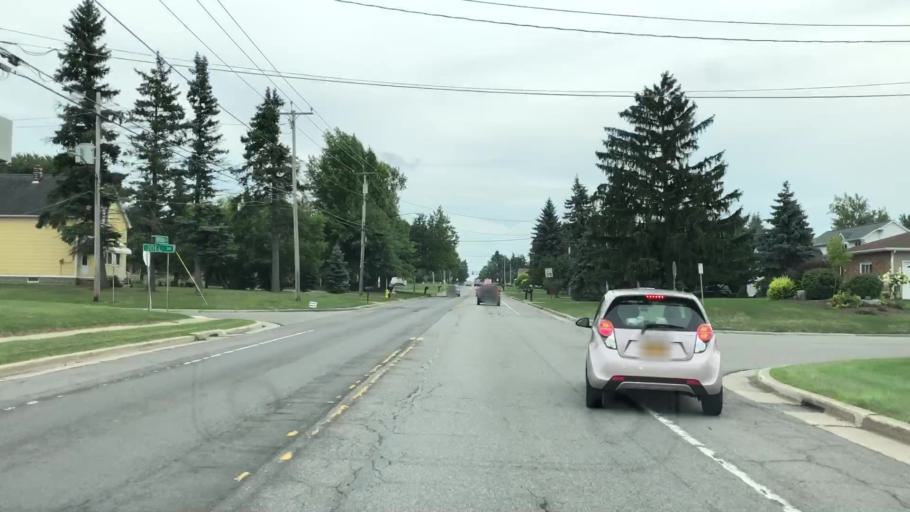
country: US
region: New York
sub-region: Erie County
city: Depew
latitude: 42.8831
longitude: -78.7091
